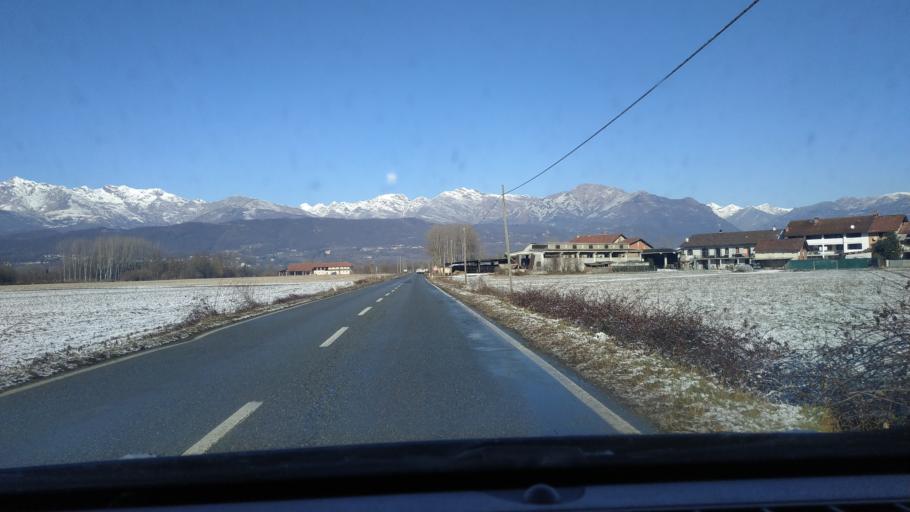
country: IT
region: Piedmont
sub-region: Provincia di Torino
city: Perosa Canavese
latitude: 45.4062
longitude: 7.8292
